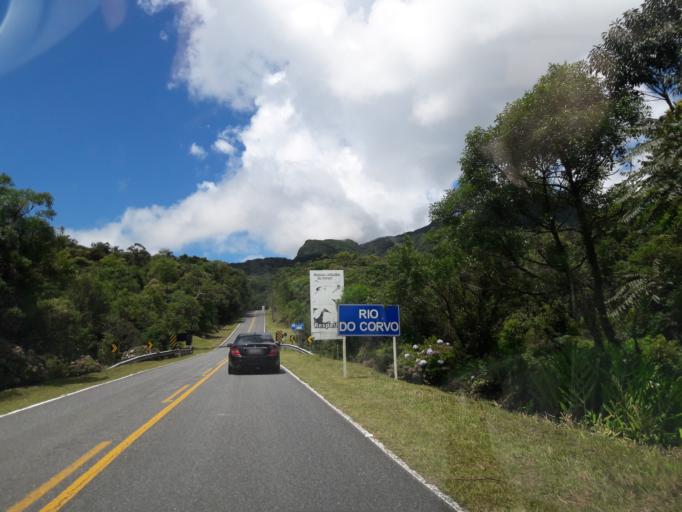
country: BR
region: Parana
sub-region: Campina Grande Do Sul
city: Campina Grande do Sul
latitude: -25.3301
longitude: -48.9136
